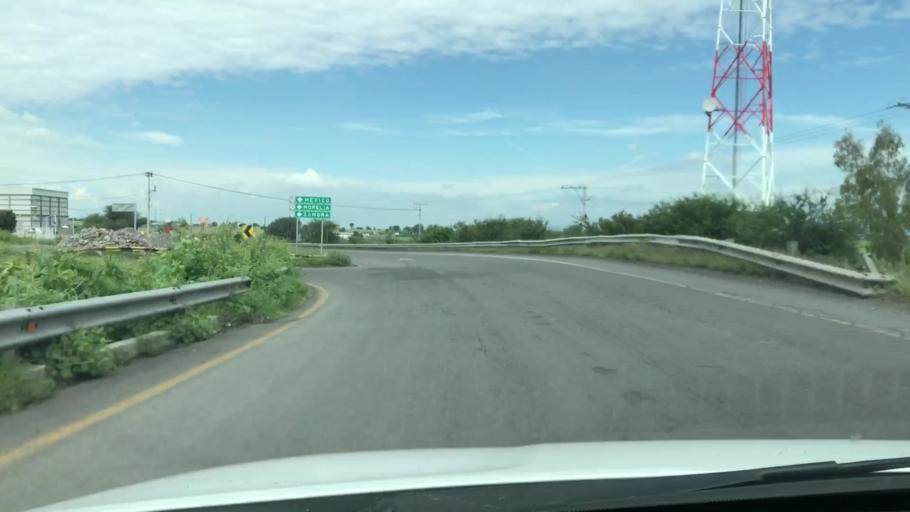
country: MX
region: Michoacan
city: Vistahermosa de Negrete
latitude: 20.2689
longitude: -102.4460
